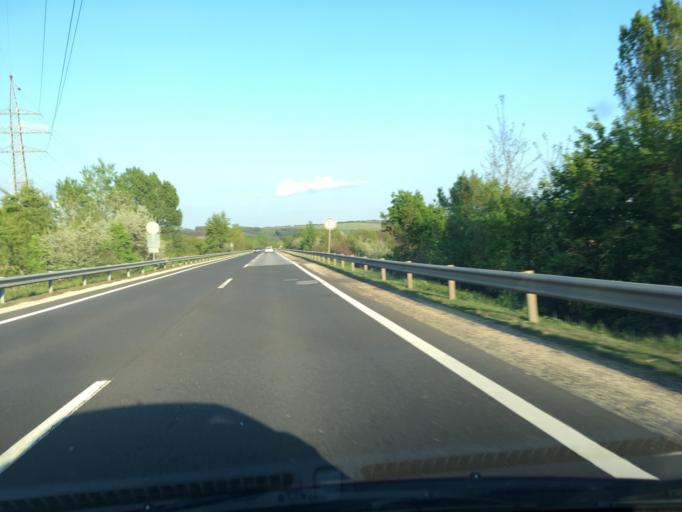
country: HU
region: Pest
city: Vac
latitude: 47.8131
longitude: 19.1101
